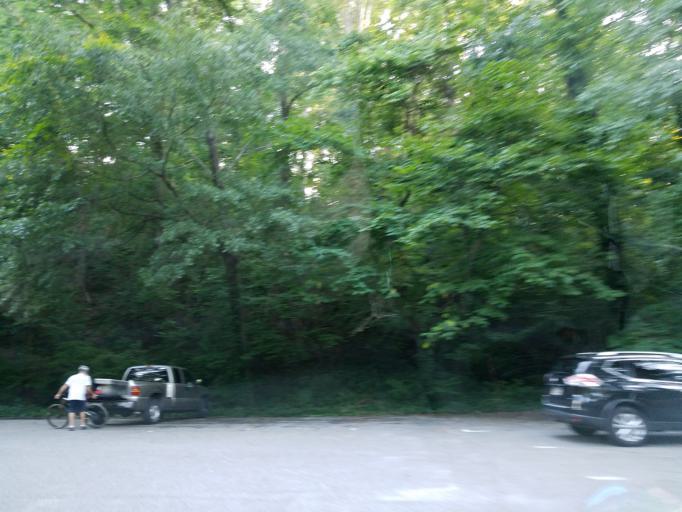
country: US
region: Georgia
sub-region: Cobb County
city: Vinings
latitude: 33.9027
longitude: -84.4446
